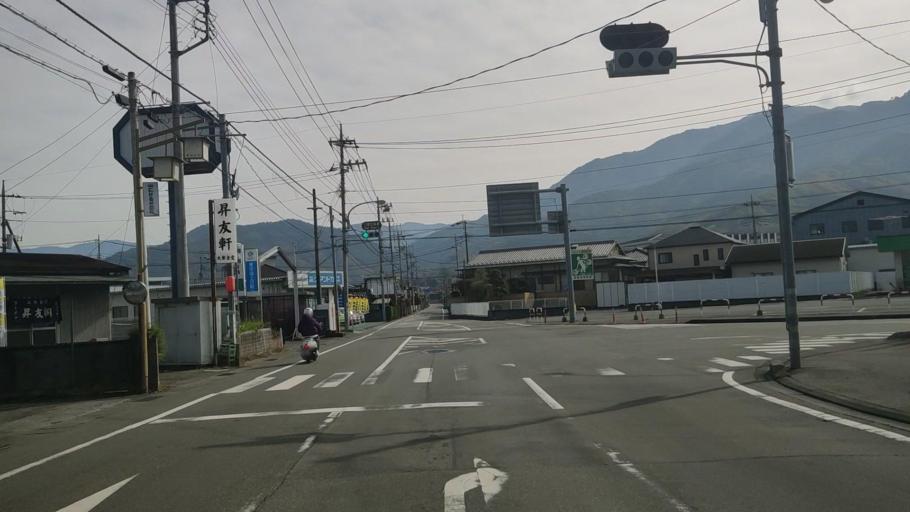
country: JP
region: Yamanashi
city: Ryuo
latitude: 35.5655
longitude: 138.4908
